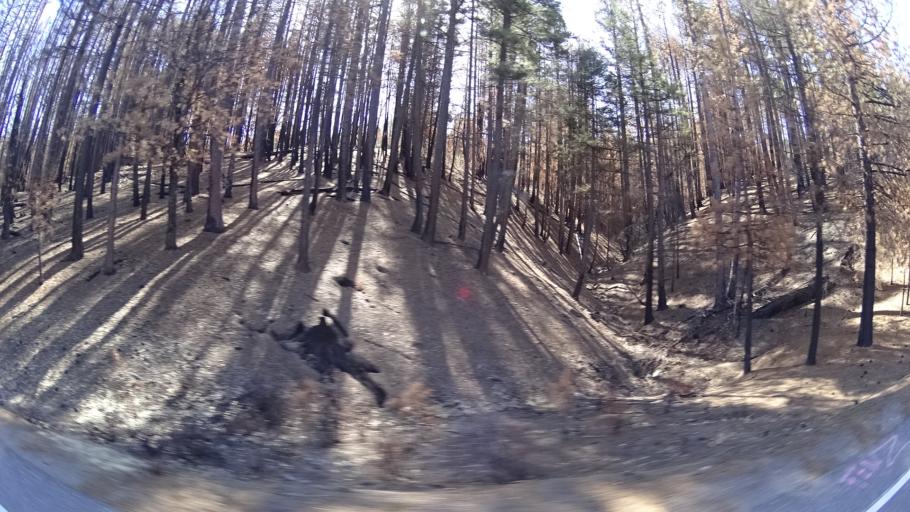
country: US
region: California
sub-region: Tehama County
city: Rancho Tehama Reserve
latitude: 39.6582
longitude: -122.7235
